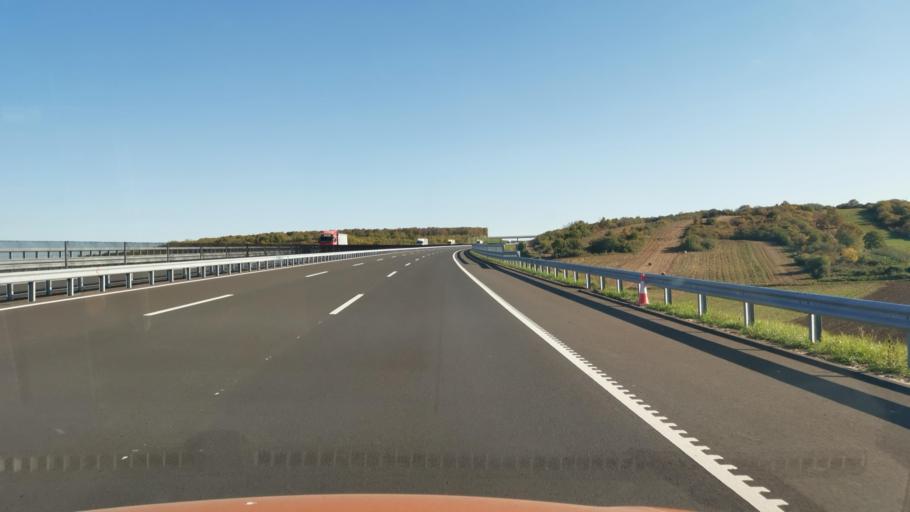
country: HU
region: Borsod-Abauj-Zemplen
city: Szikszo
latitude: 48.2107
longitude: 20.9179
